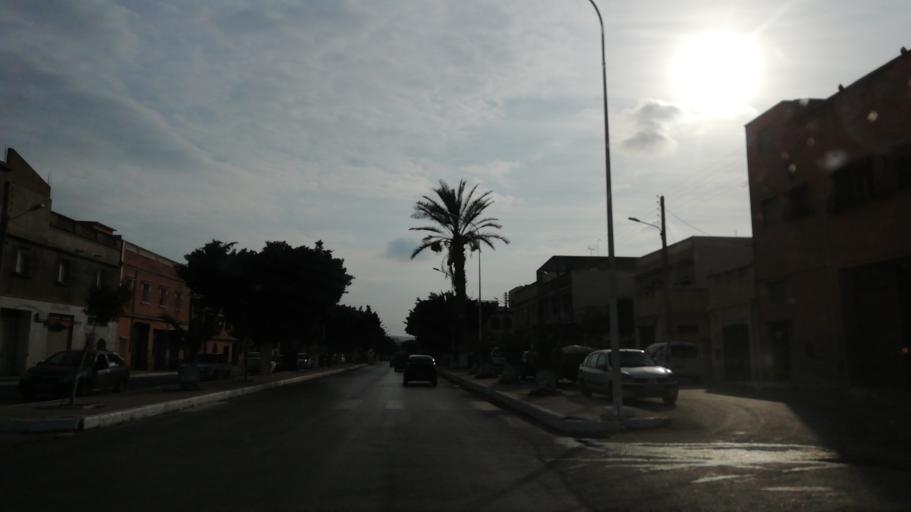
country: DZ
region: Mostaganem
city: Mostaganem
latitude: 35.8643
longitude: 0.0744
